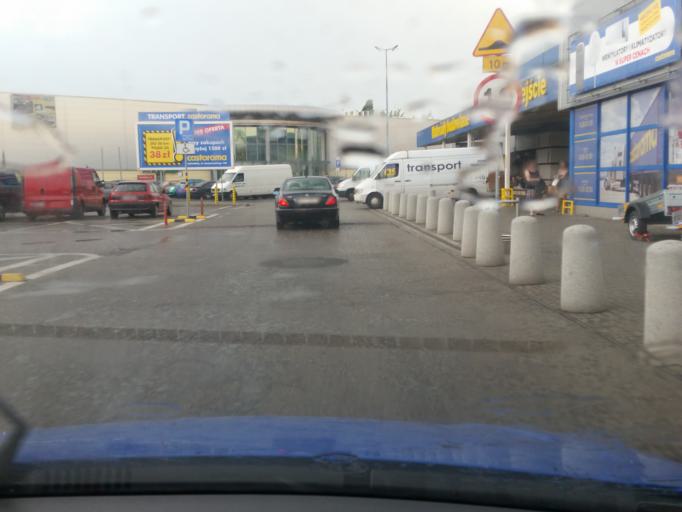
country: PL
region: Silesian Voivodeship
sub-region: Katowice
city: Katowice
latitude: 50.2685
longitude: 19.0607
